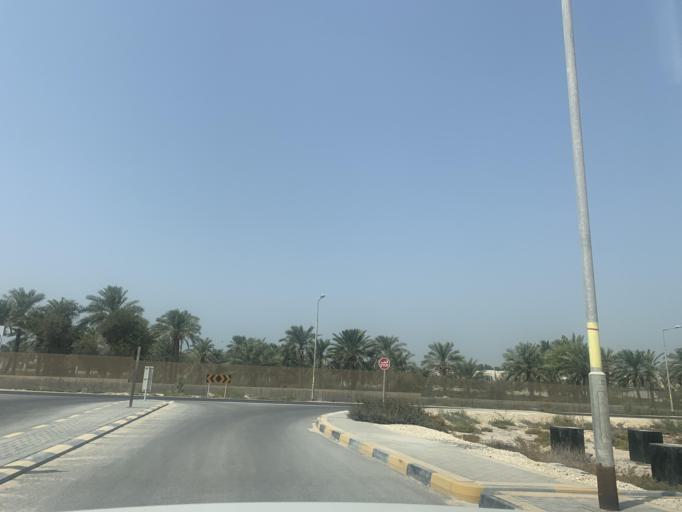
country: BH
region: Central Governorate
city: Madinat Hamad
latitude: 26.1555
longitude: 50.4701
